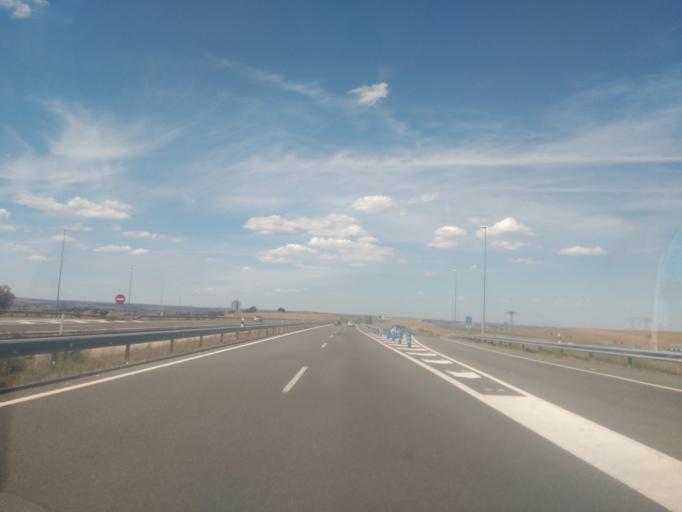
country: ES
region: Castille and Leon
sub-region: Provincia de Salamanca
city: Montejo
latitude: 40.6278
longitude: -5.6316
